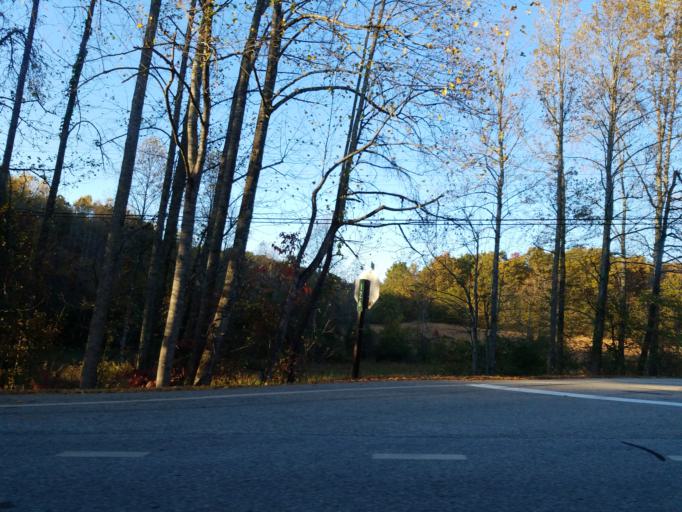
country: US
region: Georgia
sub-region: Dawson County
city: Dawsonville
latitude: 34.5494
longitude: -84.1514
